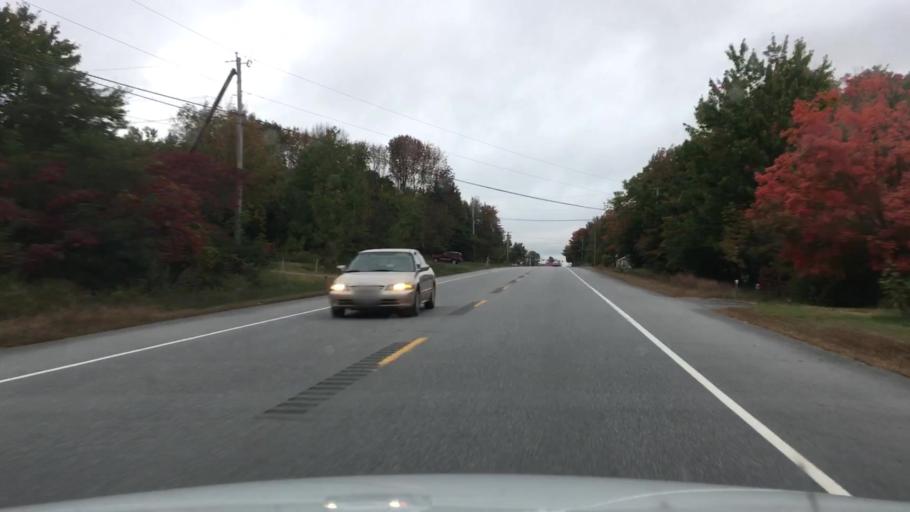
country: US
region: Maine
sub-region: Androscoggin County
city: Mechanic Falls
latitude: 44.1115
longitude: -70.4400
